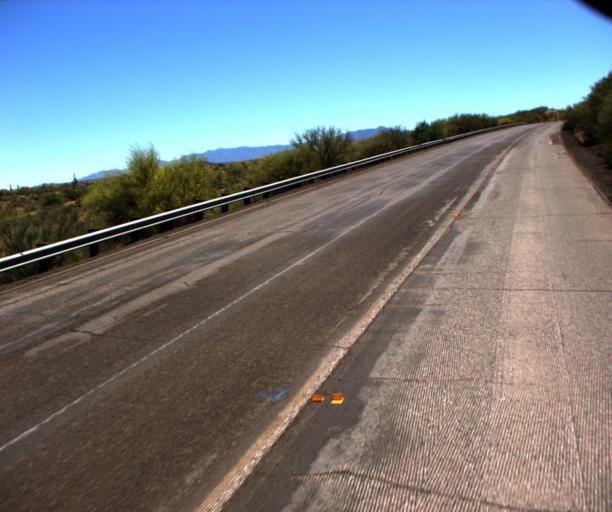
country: US
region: Arizona
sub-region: Pinal County
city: Mammoth
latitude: 32.6770
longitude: -110.6571
